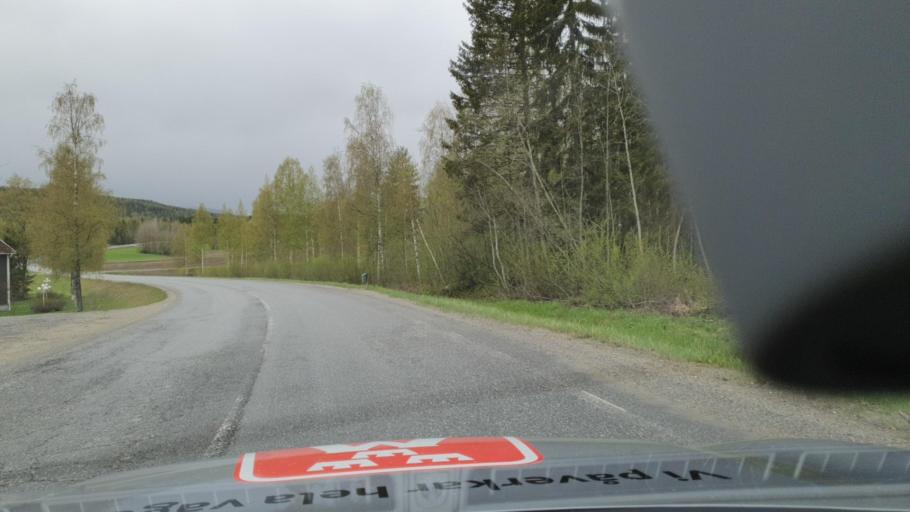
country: SE
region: Vaesternorrland
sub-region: OErnskoeldsviks Kommun
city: Bredbyn
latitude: 63.4635
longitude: 18.0145
